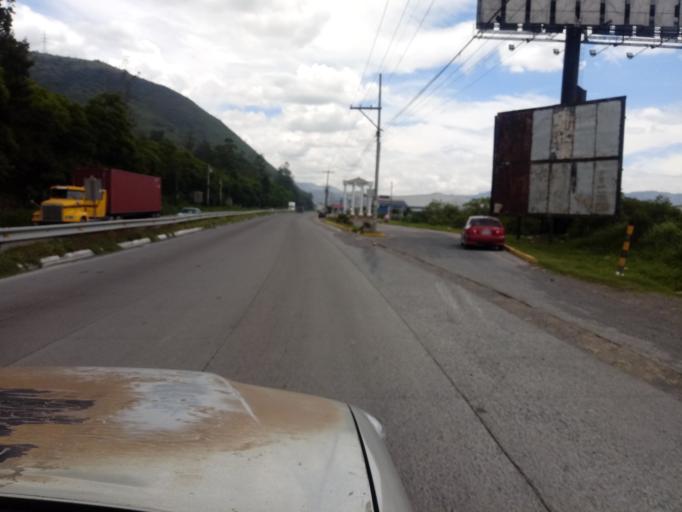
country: GT
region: Escuintla
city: San Vicente Pacaya
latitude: 14.4492
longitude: -90.6439
